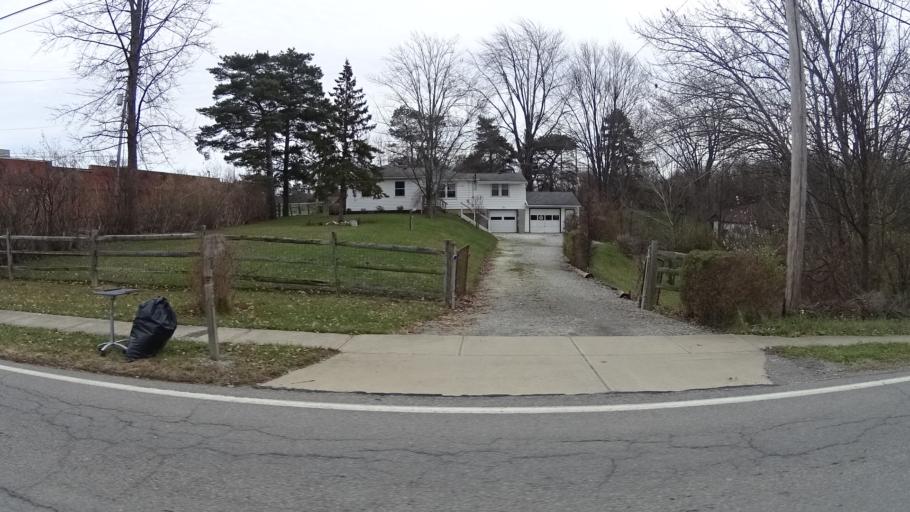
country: US
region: Ohio
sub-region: Cuyahoga County
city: Berea
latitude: 41.3497
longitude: -81.8770
